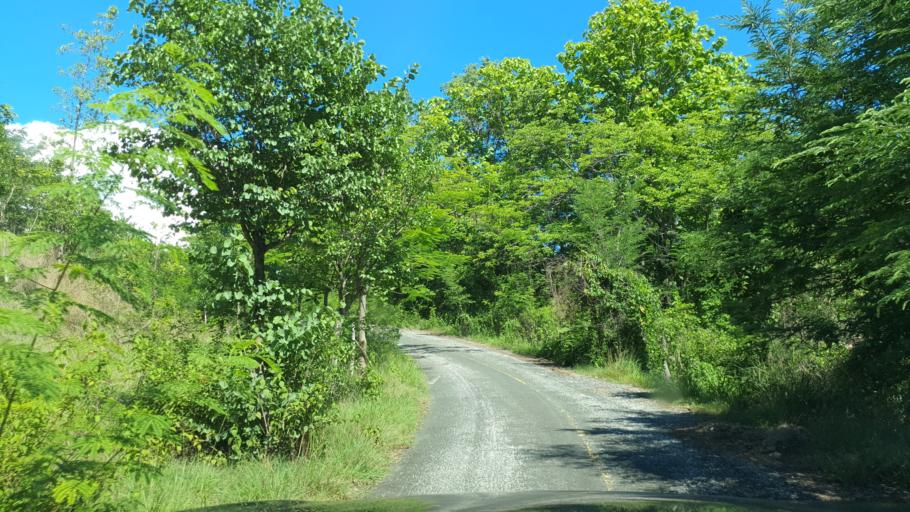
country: TH
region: Chiang Mai
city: Mae On
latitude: 18.7753
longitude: 99.2480
